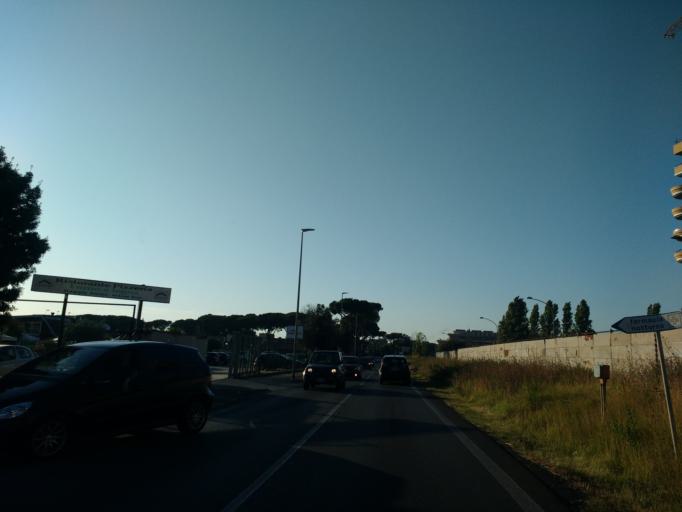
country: IT
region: Latium
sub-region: Citta metropolitana di Roma Capitale
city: Vitinia
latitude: 41.7724
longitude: 12.3722
